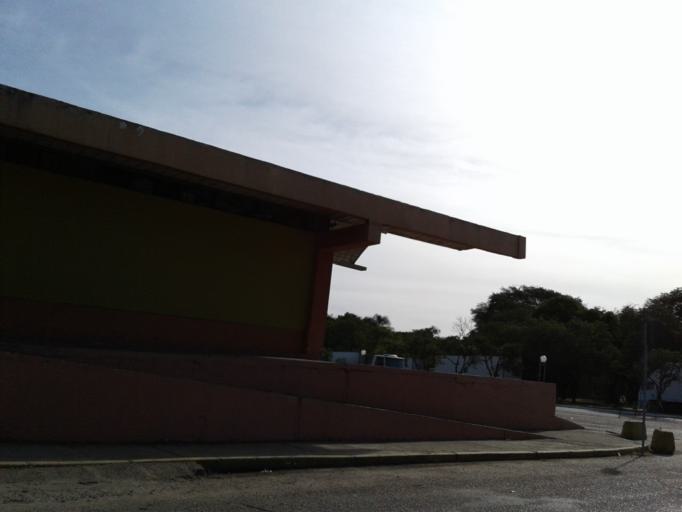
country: BR
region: Rio Grande do Sul
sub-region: Canoas
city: Canoas
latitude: -29.9764
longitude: -51.1692
